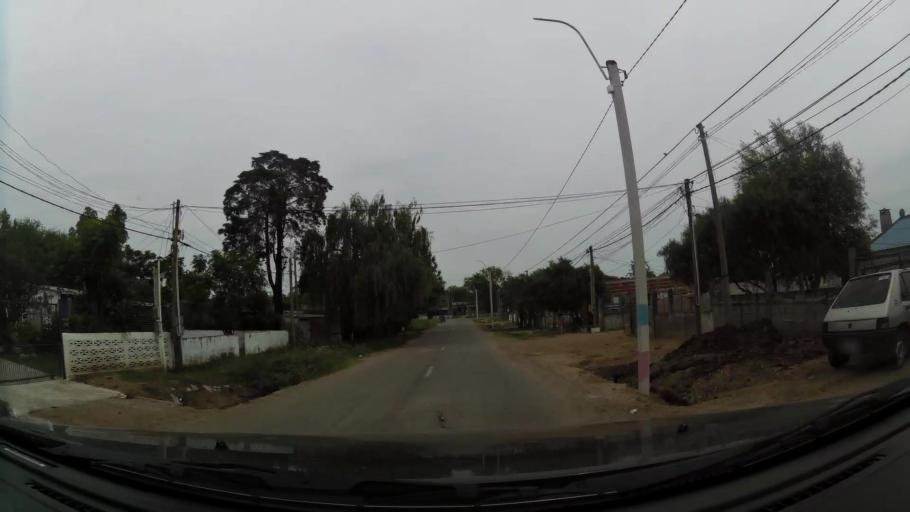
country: UY
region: Canelones
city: La Paz
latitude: -34.7432
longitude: -56.2305
